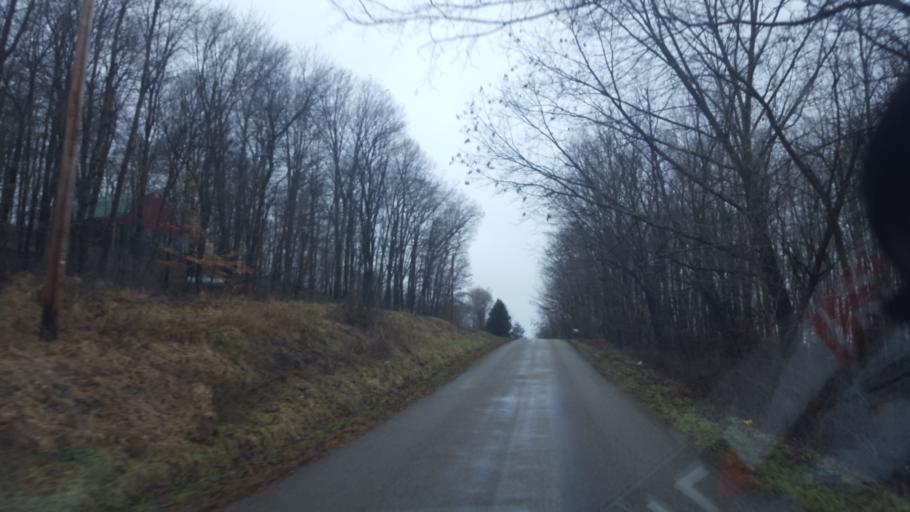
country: US
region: Ohio
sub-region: Sandusky County
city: Bellville
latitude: 40.5727
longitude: -82.3920
